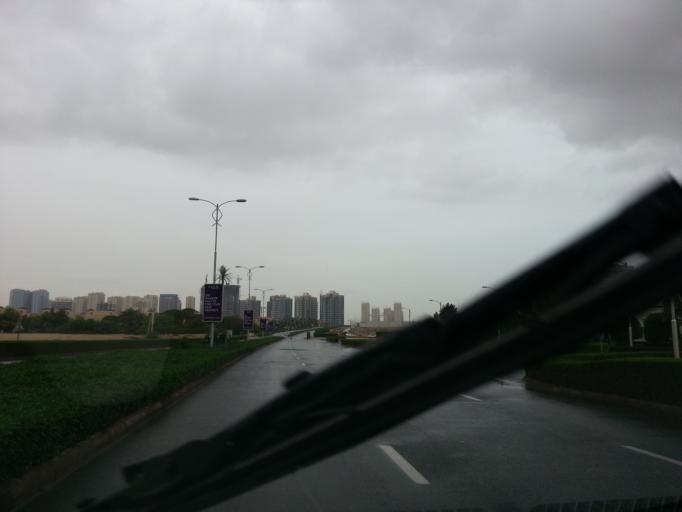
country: AE
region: Dubai
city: Dubai
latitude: 25.0456
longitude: 55.2144
